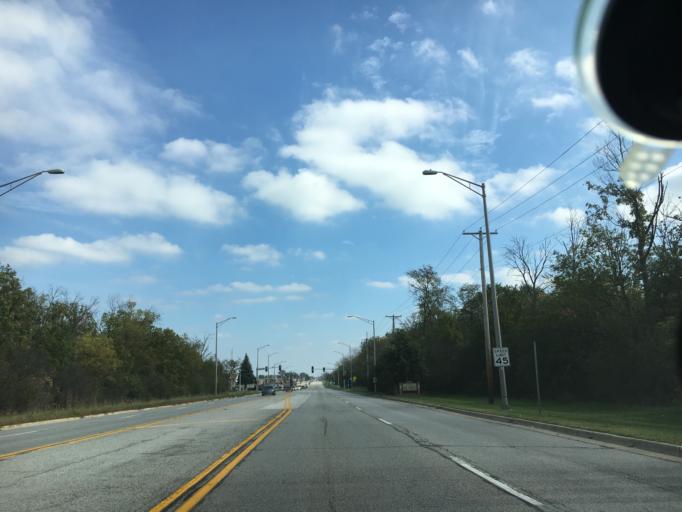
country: US
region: Illinois
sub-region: Cook County
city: Tinley Park
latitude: 41.6025
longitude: -87.7779
